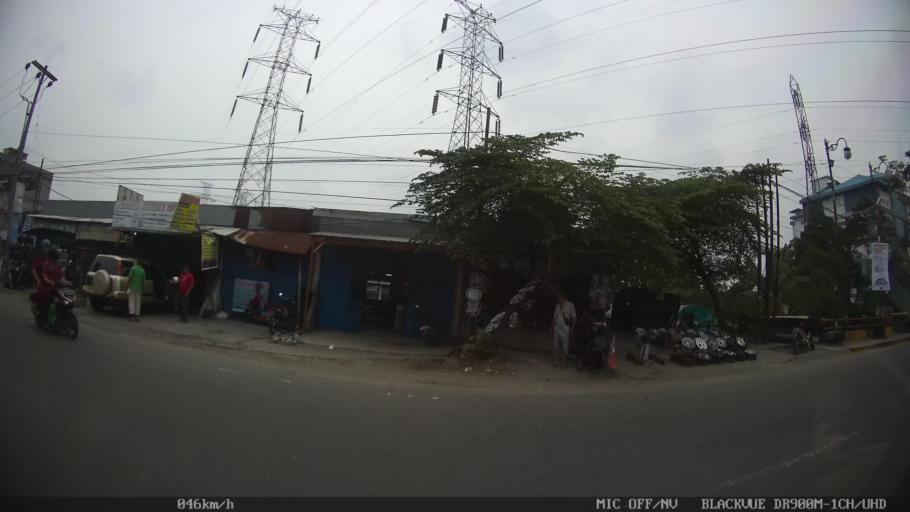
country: ID
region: North Sumatra
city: Deli Tua
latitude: 3.5382
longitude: 98.6928
